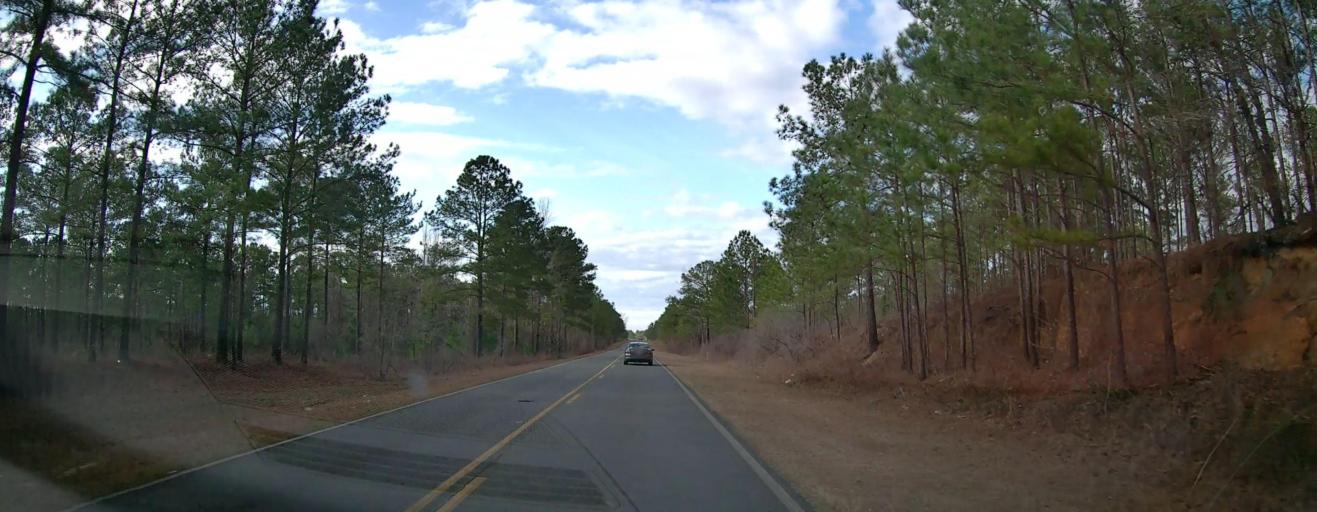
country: US
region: Georgia
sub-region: Talbot County
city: Talbotton
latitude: 32.5031
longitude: -84.5841
